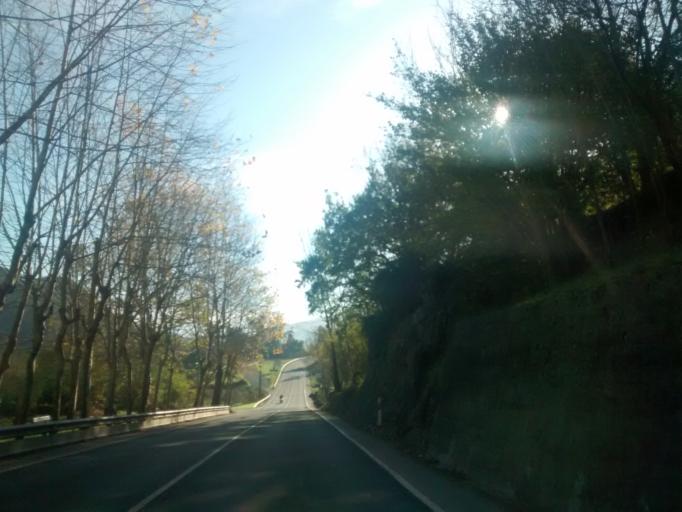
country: ES
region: Cantabria
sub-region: Provincia de Cantabria
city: Puente Viesgo
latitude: 43.2951
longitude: -3.9652
